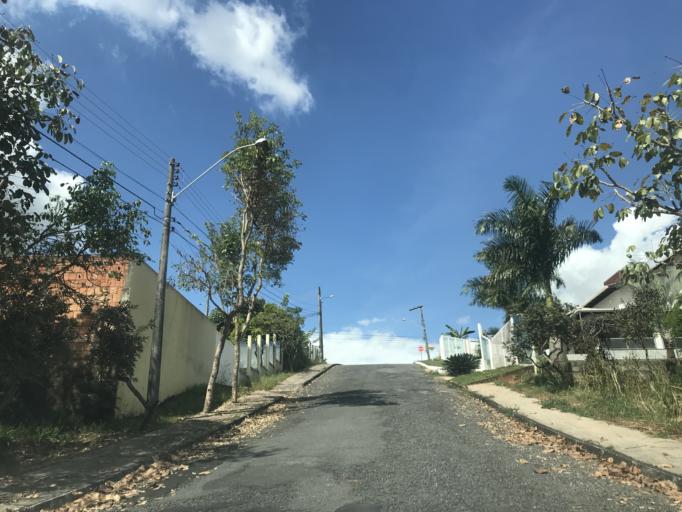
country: BR
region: Federal District
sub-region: Brasilia
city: Brasilia
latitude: -15.8658
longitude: -47.7480
